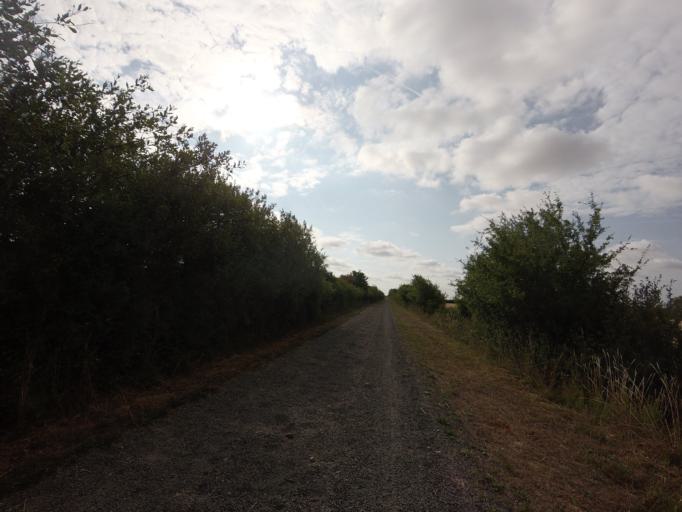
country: SE
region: Skane
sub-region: Helsingborg
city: Odakra
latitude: 56.1644
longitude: 12.7356
